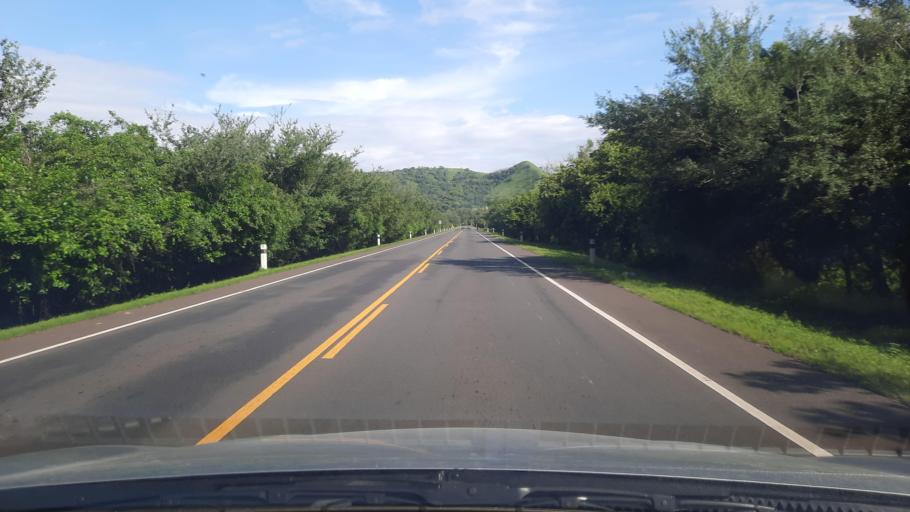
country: NI
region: Leon
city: Telica
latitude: 12.7055
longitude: -86.8711
